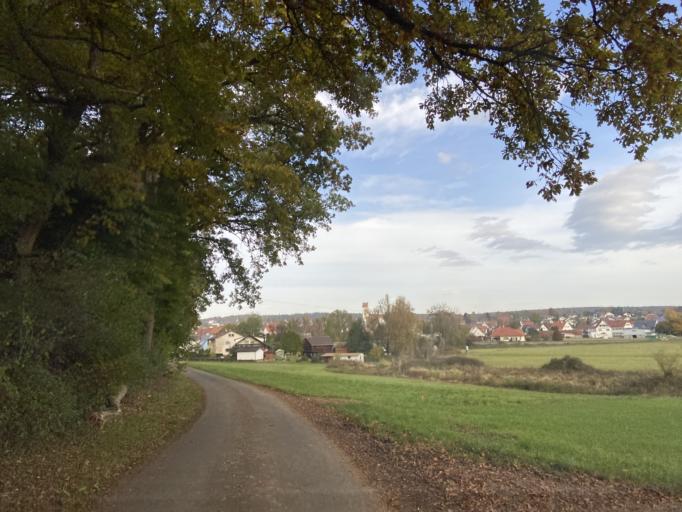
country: DE
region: Baden-Wuerttemberg
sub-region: Tuebingen Region
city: Bingen
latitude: 48.1054
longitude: 9.2796
